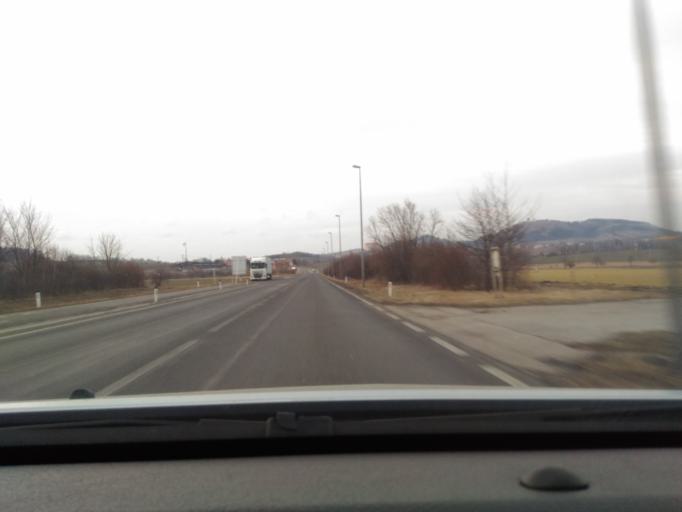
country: CZ
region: South Moravian
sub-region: Okres Breclav
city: Mikulov
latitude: 48.7826
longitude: 16.6395
